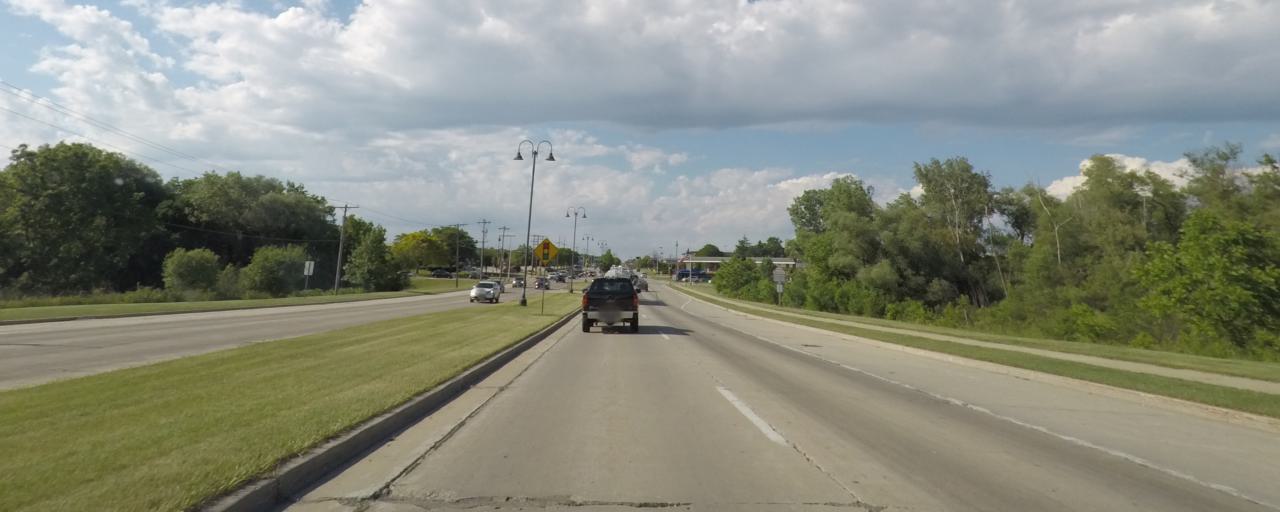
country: US
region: Wisconsin
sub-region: Milwaukee County
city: Greendale
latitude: 42.9432
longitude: -88.0085
